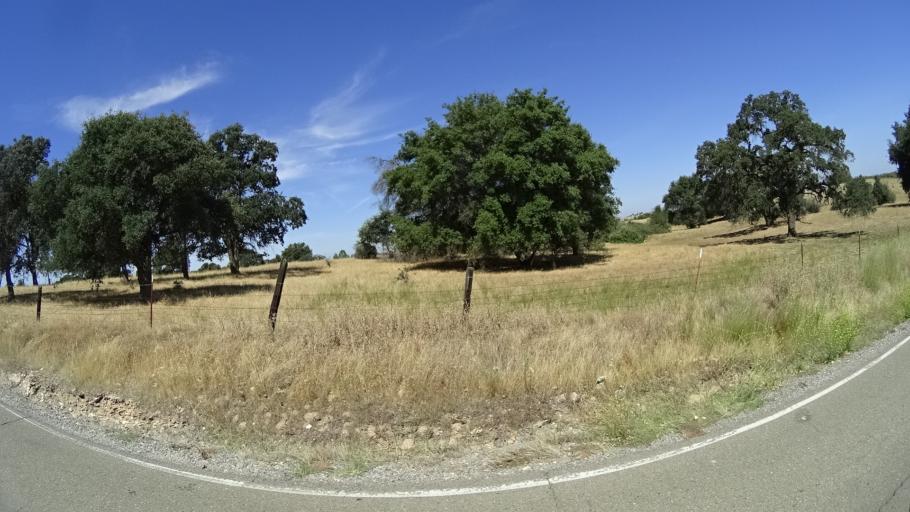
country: US
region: California
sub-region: Calaveras County
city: Rancho Calaveras
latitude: 38.1343
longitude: -120.8994
